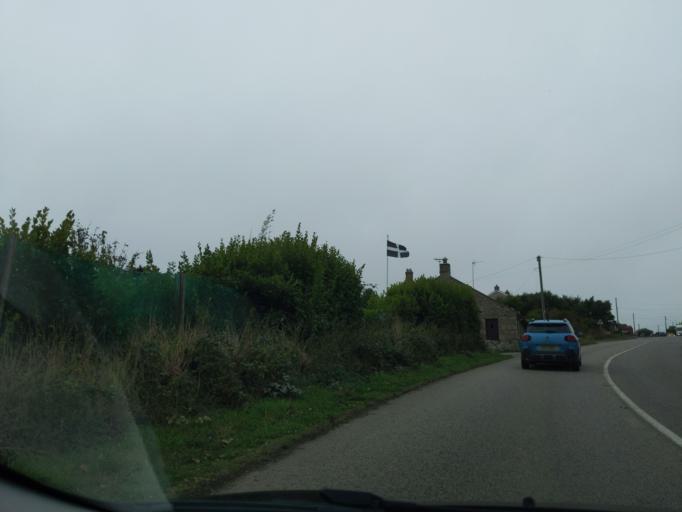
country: GB
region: England
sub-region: Cornwall
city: Germoe
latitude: 50.1075
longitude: -5.3506
